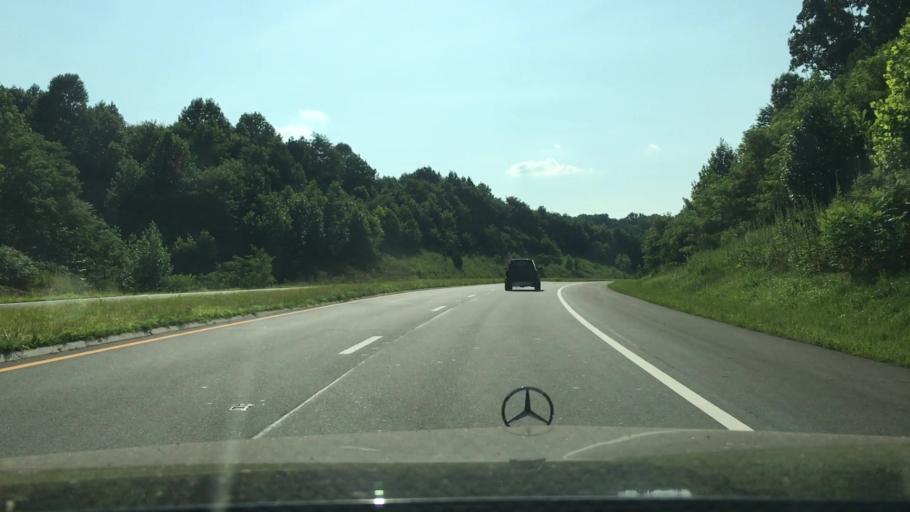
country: US
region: Virginia
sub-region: Amherst County
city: Madison Heights
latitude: 37.4142
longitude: -79.1070
